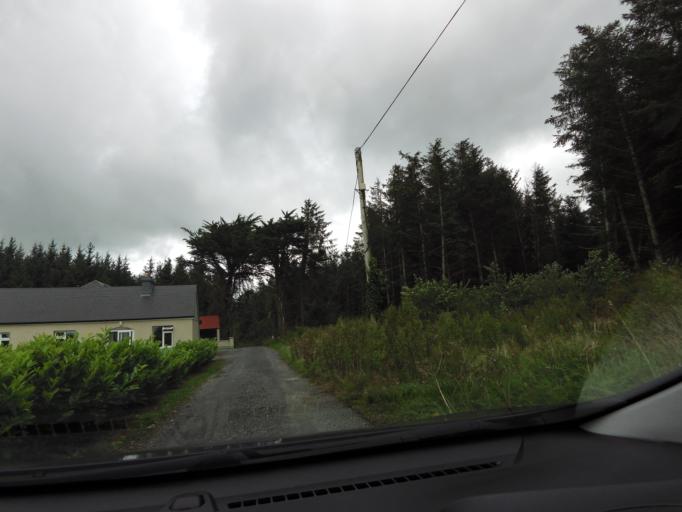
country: IE
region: Connaught
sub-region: County Galway
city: Athenry
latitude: 53.3071
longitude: -8.6986
